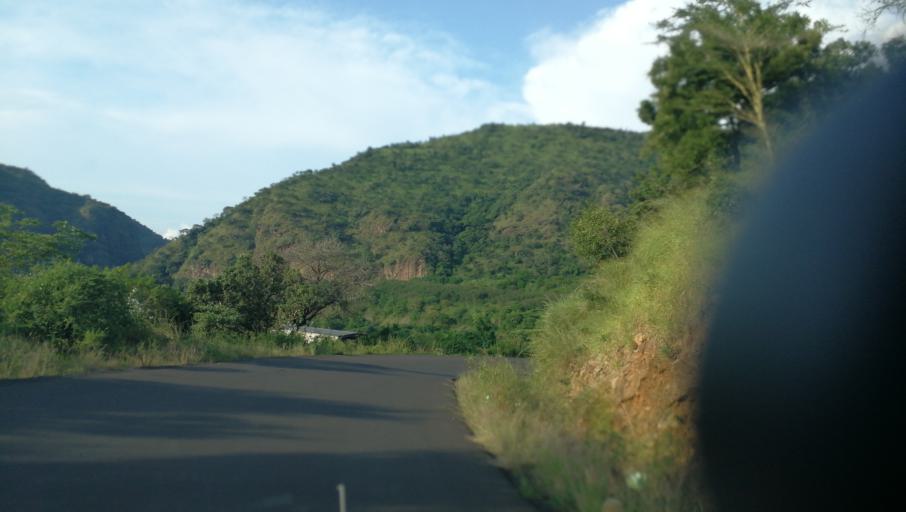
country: ET
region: Southern Nations, Nationalities, and People's Region
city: Areka
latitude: 6.8283
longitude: 37.2953
